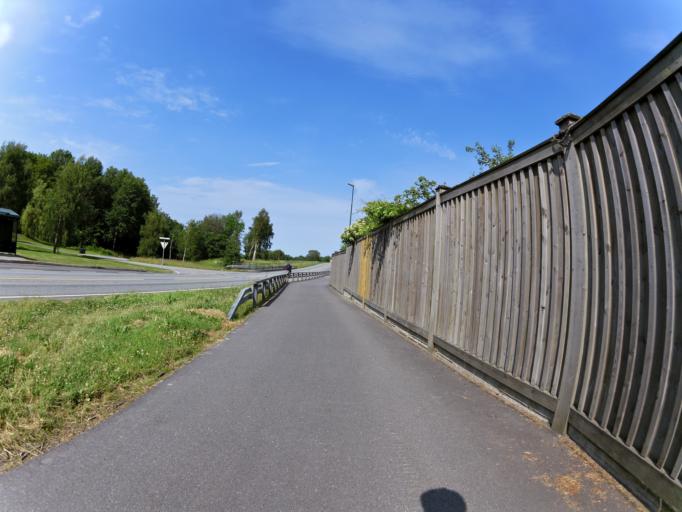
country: NO
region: Ostfold
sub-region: Sarpsborg
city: Sarpsborg
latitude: 59.2677
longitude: 11.1249
